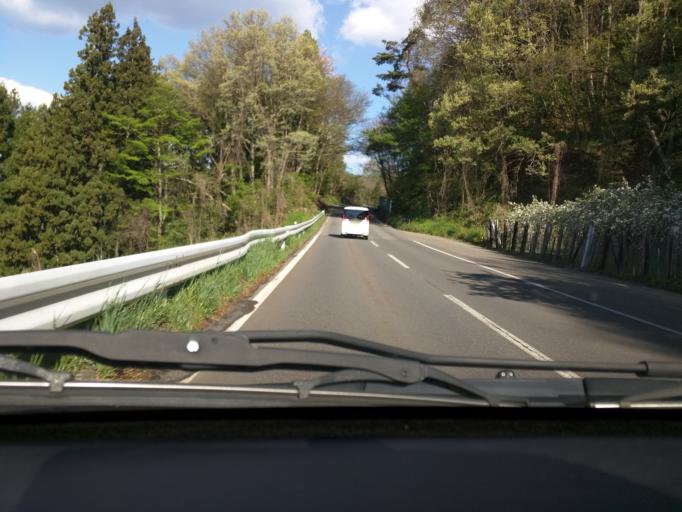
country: JP
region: Nagano
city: Nagano-shi
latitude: 36.6831
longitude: 138.1637
